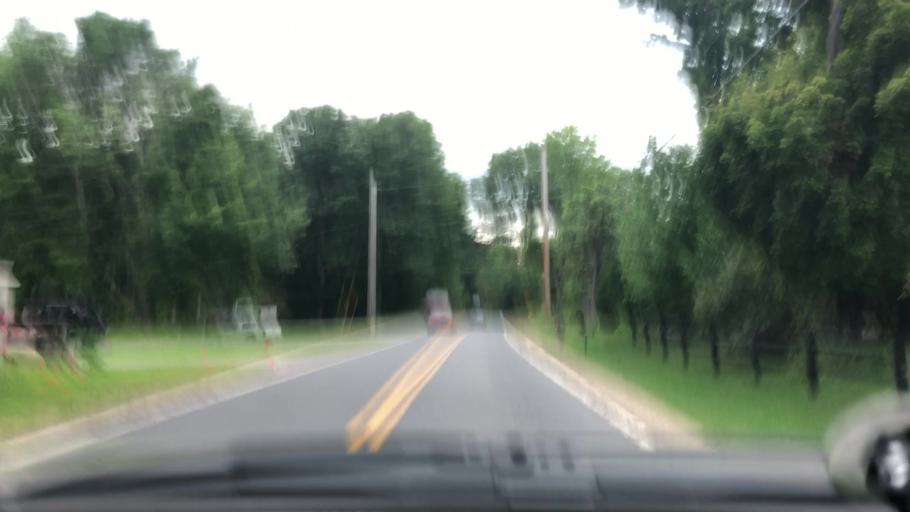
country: US
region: New York
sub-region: Saratoga County
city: Corinth
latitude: 43.2134
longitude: -73.7999
